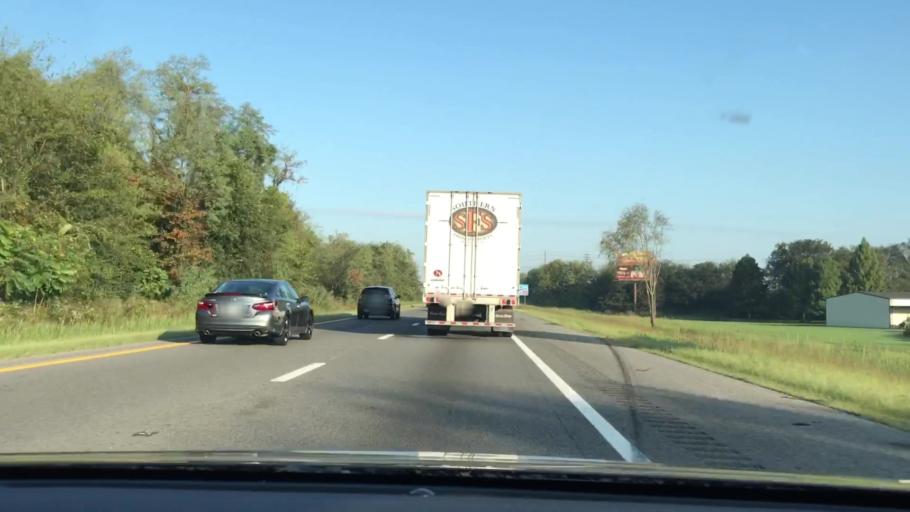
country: US
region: Tennessee
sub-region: Montgomery County
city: Clarksville
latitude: 36.5769
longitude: -87.2618
